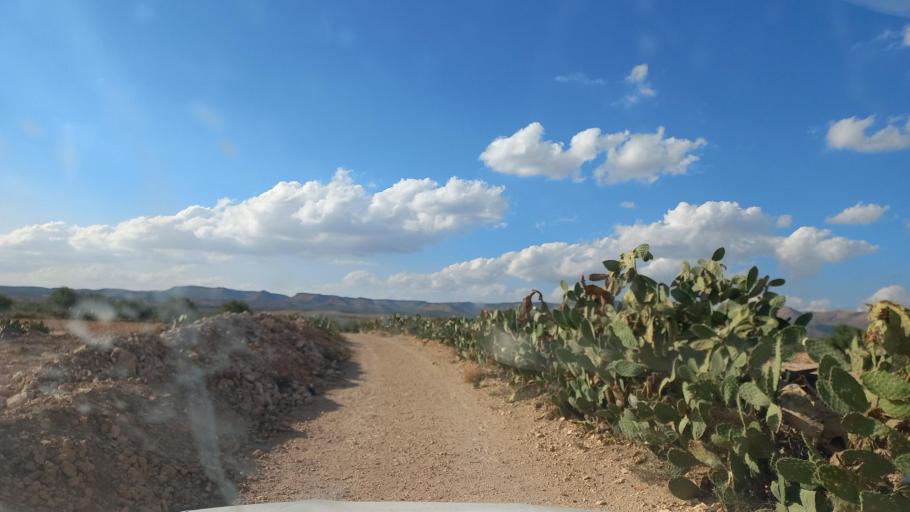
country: TN
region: Al Qasrayn
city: Sbiba
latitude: 35.3846
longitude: 9.0424
